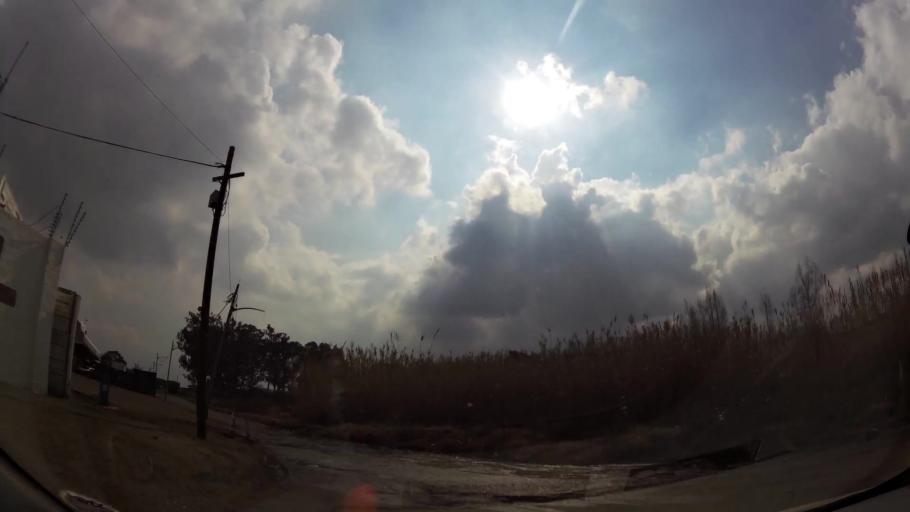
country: ZA
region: Gauteng
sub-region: Sedibeng District Municipality
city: Vereeniging
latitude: -26.6639
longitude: 27.9324
